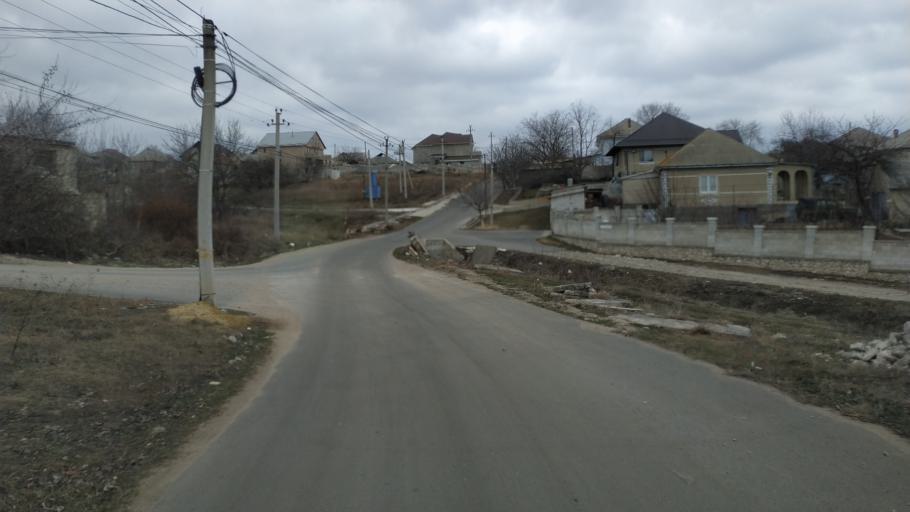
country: MD
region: Laloveni
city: Ialoveni
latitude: 46.9261
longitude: 28.7786
